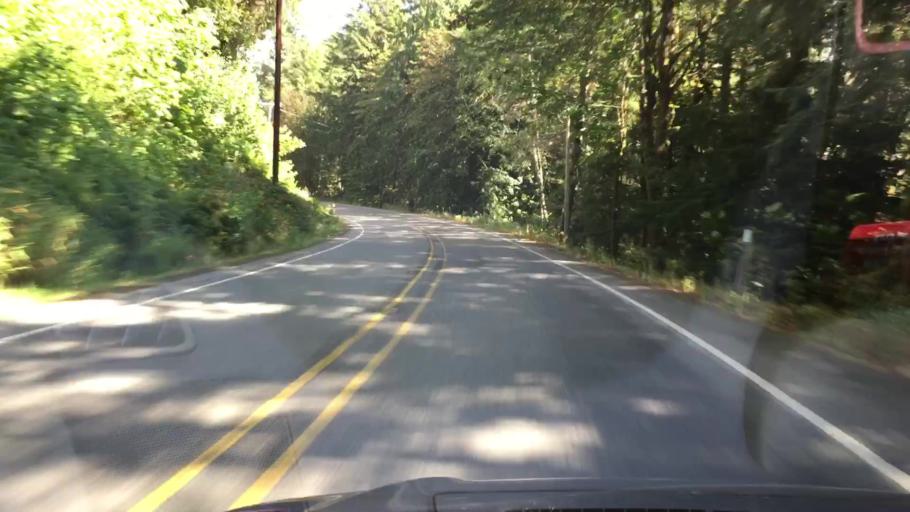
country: US
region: Washington
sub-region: Pierce County
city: Eatonville
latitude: 46.7557
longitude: -121.9712
